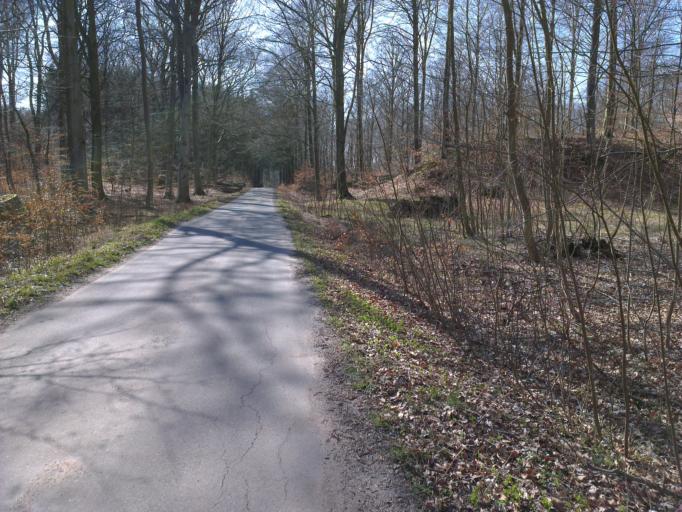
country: DK
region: Capital Region
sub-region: Frederikssund Kommune
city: Jaegerspris
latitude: 55.8828
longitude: 11.9966
